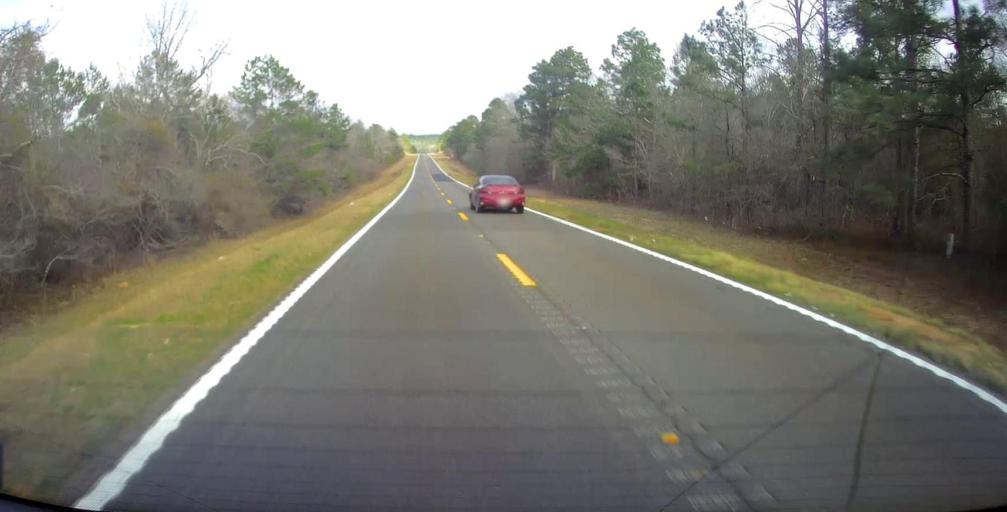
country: US
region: Georgia
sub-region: Marion County
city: Buena Vista
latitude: 32.4386
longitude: -84.5010
